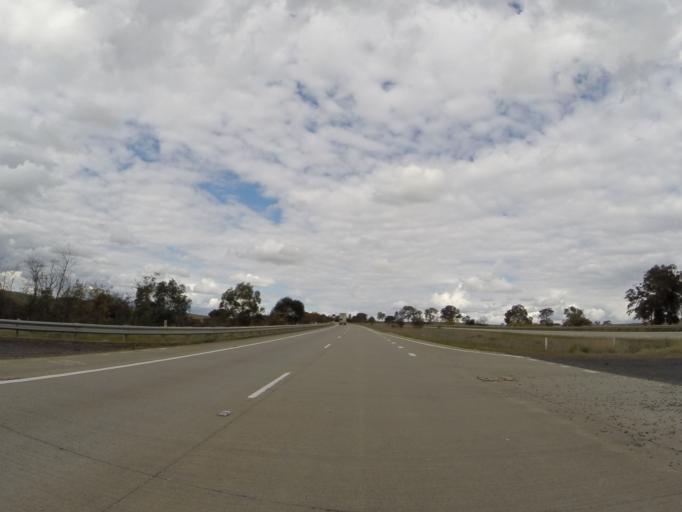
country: AU
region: New South Wales
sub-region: Yass Valley
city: Gundaroo
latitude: -34.8096
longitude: 149.3132
